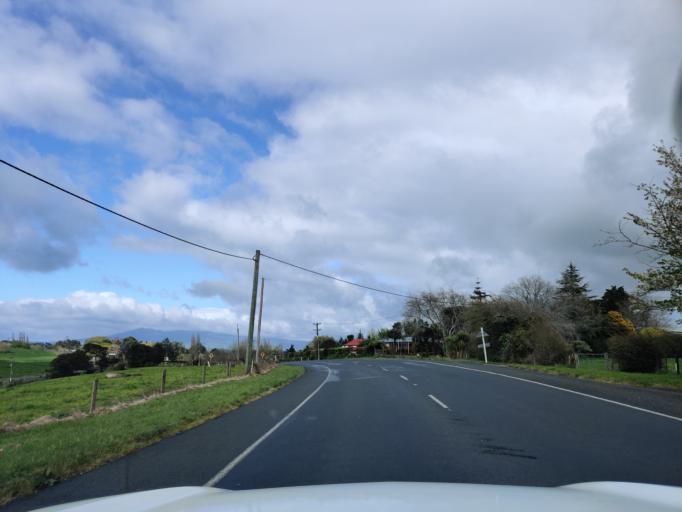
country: NZ
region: Waikato
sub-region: Hamilton City
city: Hamilton
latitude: -37.8299
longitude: 175.2193
